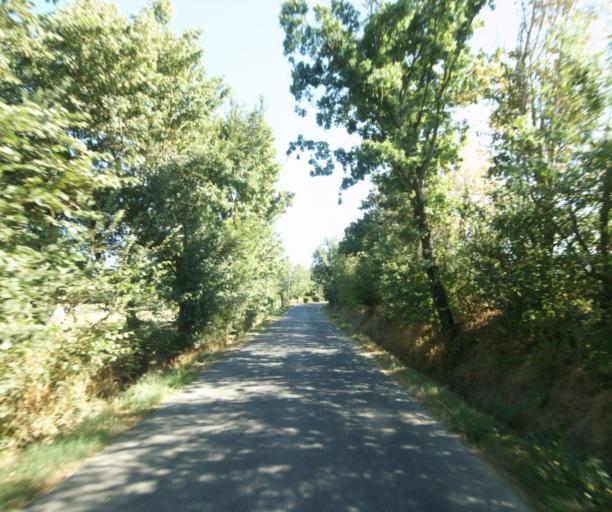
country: FR
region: Midi-Pyrenees
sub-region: Departement de la Haute-Garonne
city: Revel
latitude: 43.4982
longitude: 1.9452
